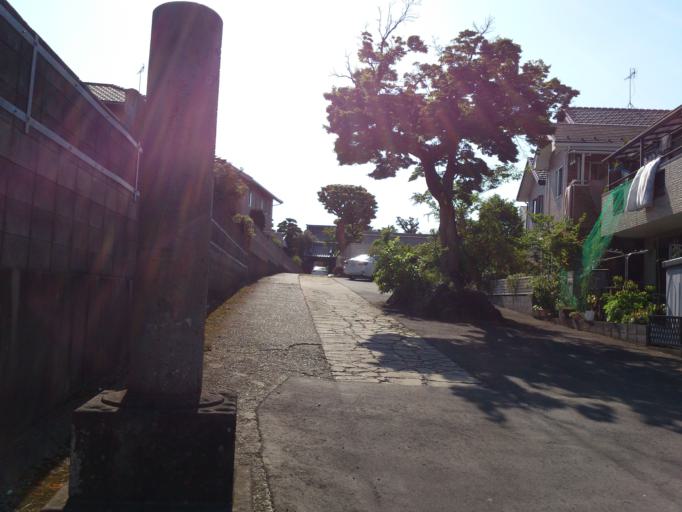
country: JP
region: Chiba
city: Matsudo
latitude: 35.7625
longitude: 139.8980
